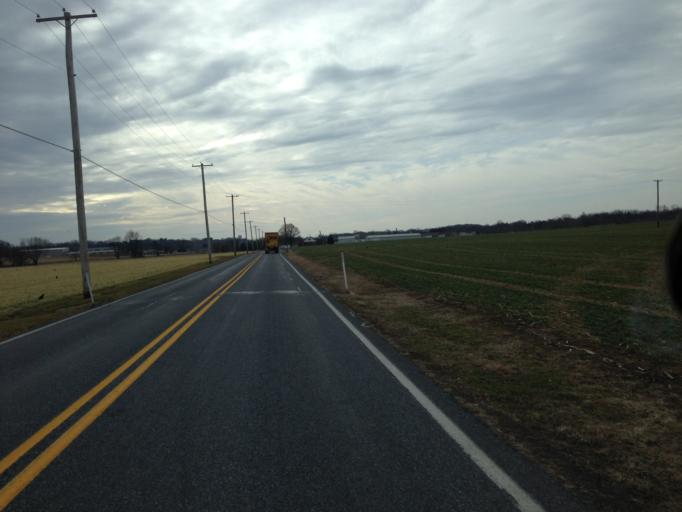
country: US
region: Pennsylvania
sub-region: Lancaster County
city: Manheim
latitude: 40.1653
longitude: -76.3758
